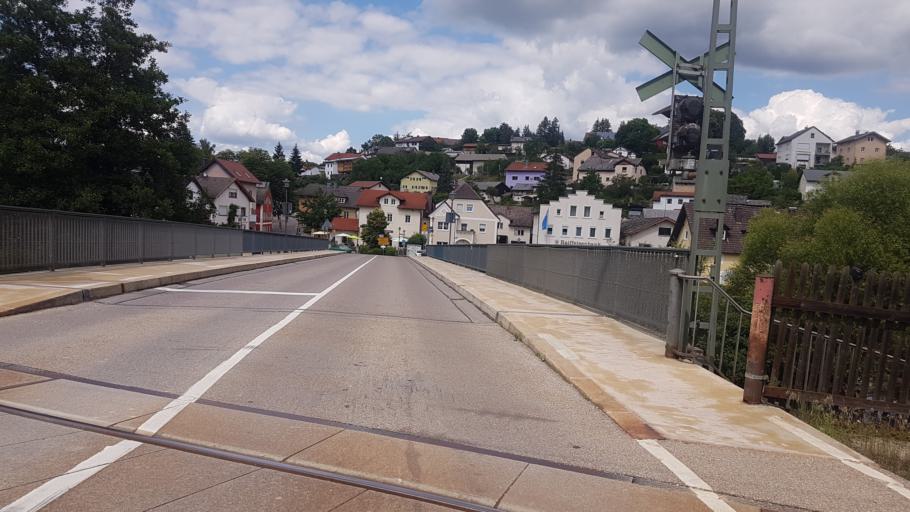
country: DE
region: Bavaria
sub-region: Regierungsbezirk Mittelfranken
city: Solnhofen
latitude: 48.8940
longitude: 10.9909
